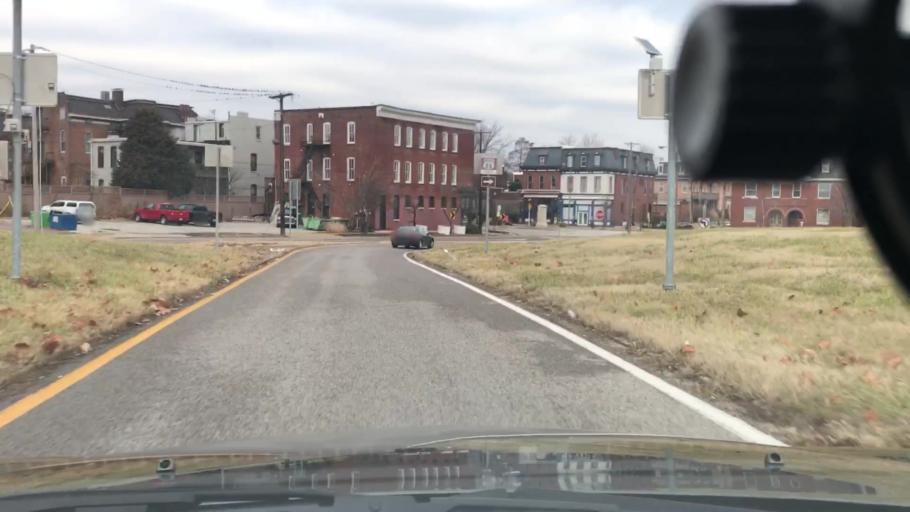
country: US
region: Missouri
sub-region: City of Saint Louis
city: St. Louis
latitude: 38.6127
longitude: -90.2115
